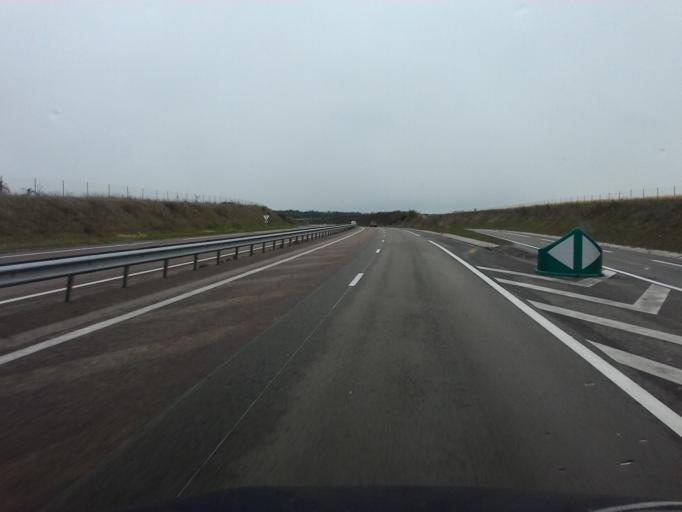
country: FR
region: Champagne-Ardenne
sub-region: Departement de la Haute-Marne
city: Chaumont
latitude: 48.1331
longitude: 5.1096
